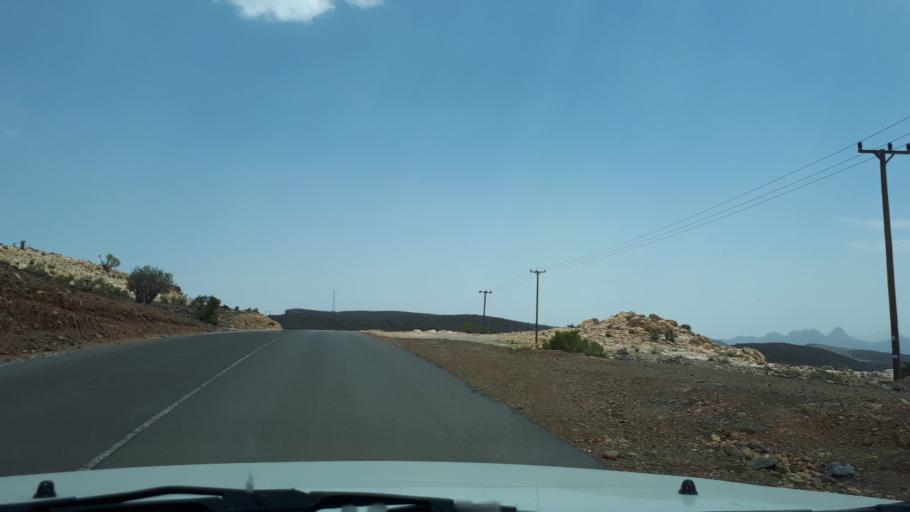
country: OM
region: Al Batinah
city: Rustaq
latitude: 23.2340
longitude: 57.1982
